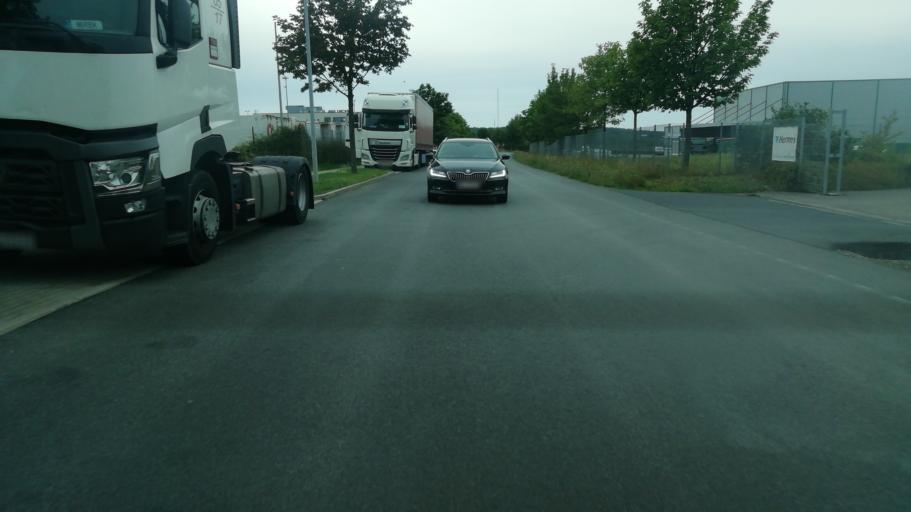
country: DE
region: Saxony
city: Wilsdruff
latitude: 51.0596
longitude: 13.5434
